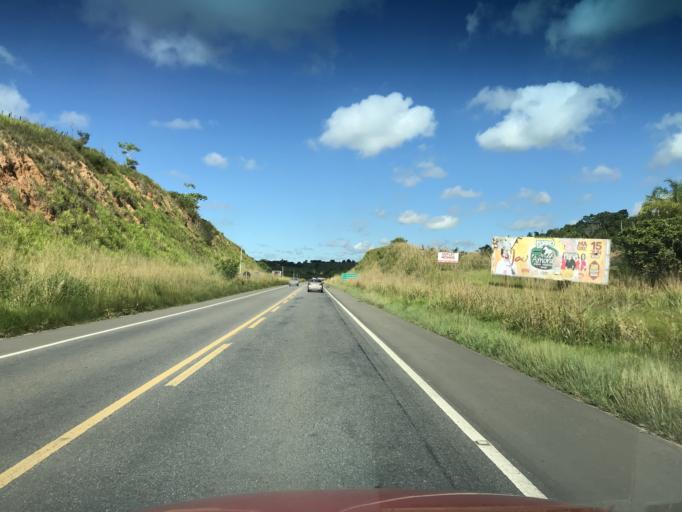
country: BR
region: Bahia
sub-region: Conceicao Do Almeida
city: Muritiba
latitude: -12.9270
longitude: -39.2518
